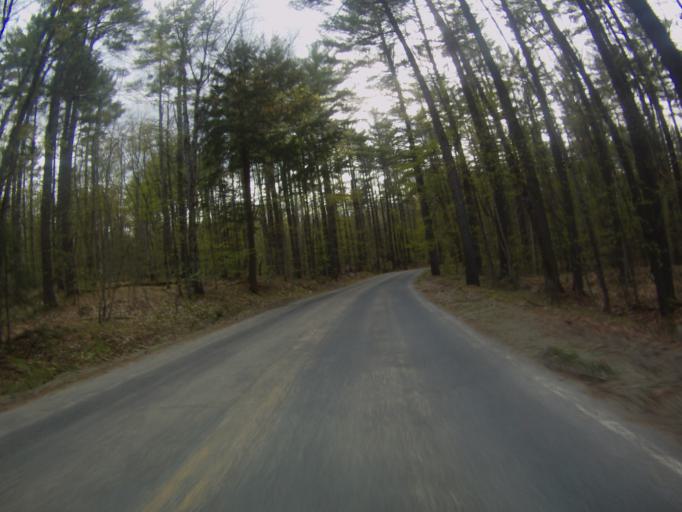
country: US
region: New York
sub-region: Warren County
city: Warrensburg
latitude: 43.8256
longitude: -73.9071
